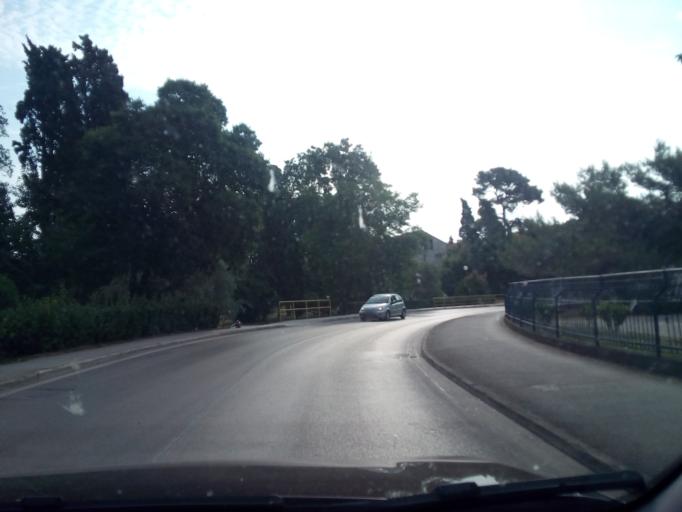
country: HR
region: Zadarska
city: Zadar
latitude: 44.1201
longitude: 15.2303
